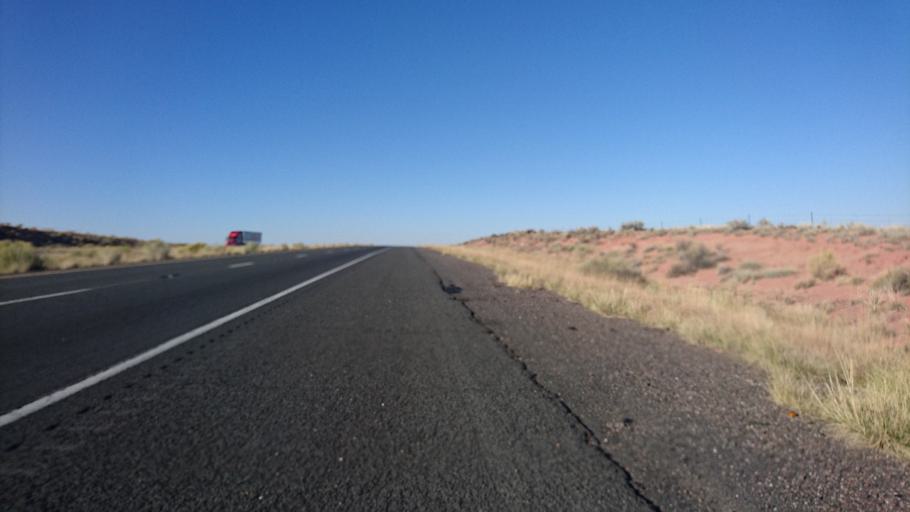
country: US
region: Arizona
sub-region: Apache County
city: Houck
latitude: 35.1056
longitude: -109.6078
